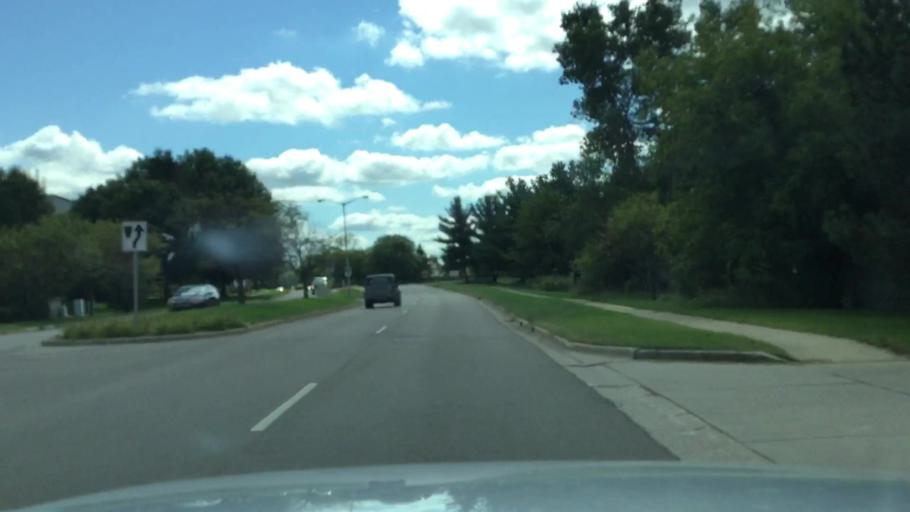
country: US
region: Michigan
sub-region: Kalamazoo County
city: Portage
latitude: 42.2288
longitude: -85.6017
